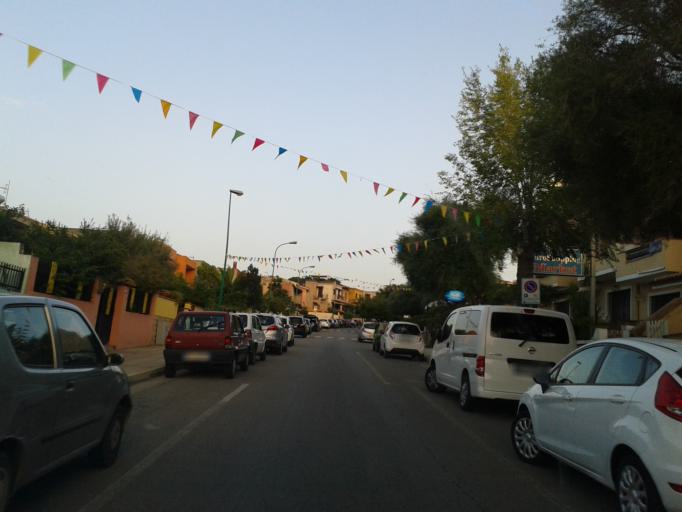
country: IT
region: Sardinia
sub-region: Provincia di Cagliari
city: Villasimius
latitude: 39.1454
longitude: 9.5121
